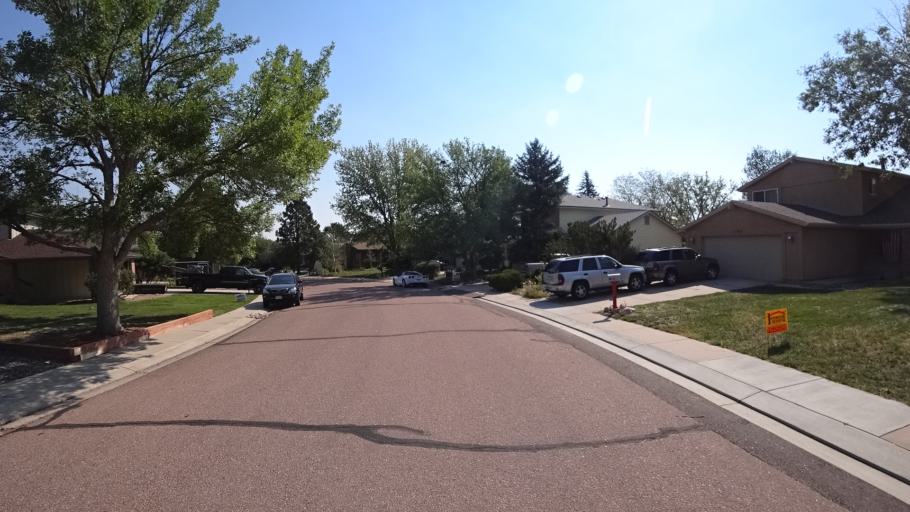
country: US
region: Colorado
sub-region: El Paso County
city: Stratmoor
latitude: 38.7858
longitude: -104.8185
